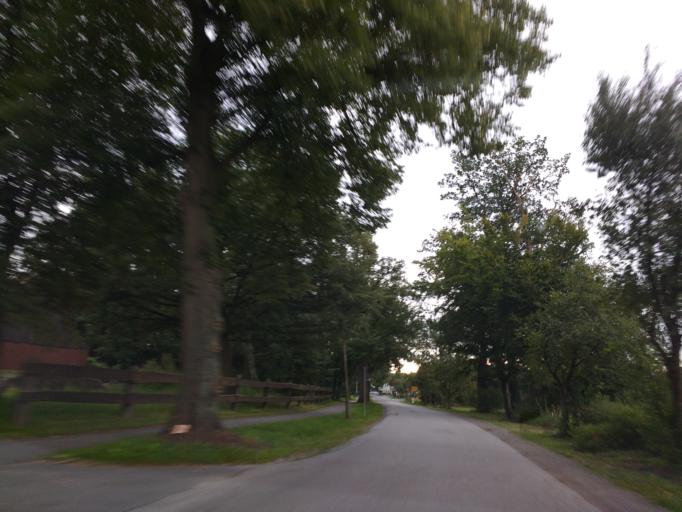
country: DE
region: North Rhine-Westphalia
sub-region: Regierungsbezirk Detmold
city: Delbruck
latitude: 51.8186
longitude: 8.5539
